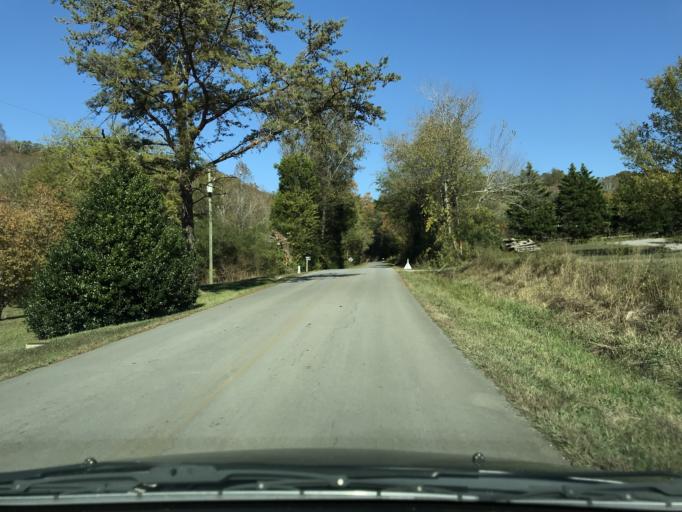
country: US
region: Georgia
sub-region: Dade County
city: Trenton
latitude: 34.9021
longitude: -85.4632
